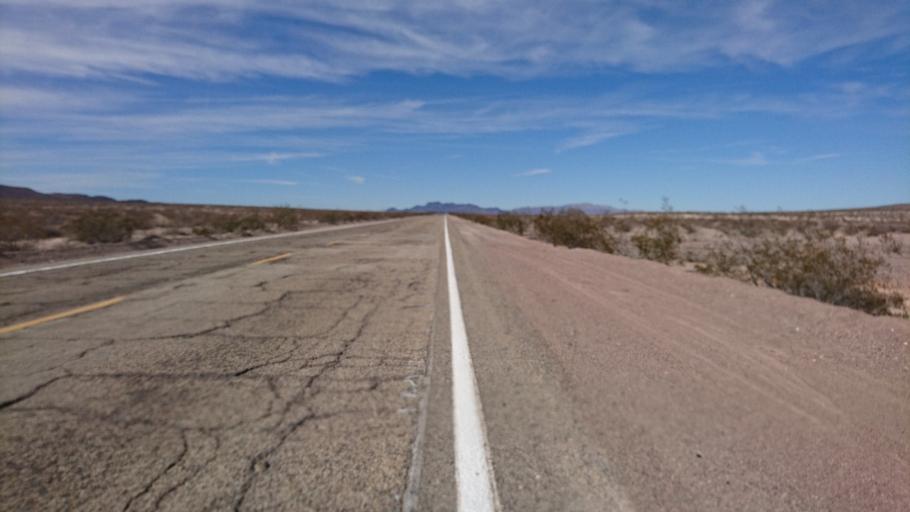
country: US
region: California
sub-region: San Bernardino County
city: Twentynine Palms
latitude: 34.7044
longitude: -116.0744
